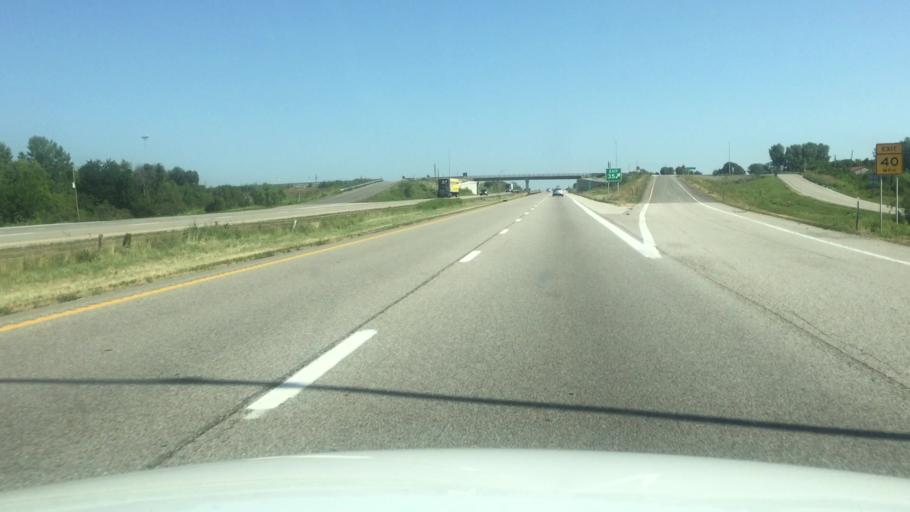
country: US
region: Kansas
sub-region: Doniphan County
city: Elwood
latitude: 39.5966
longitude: -94.7886
